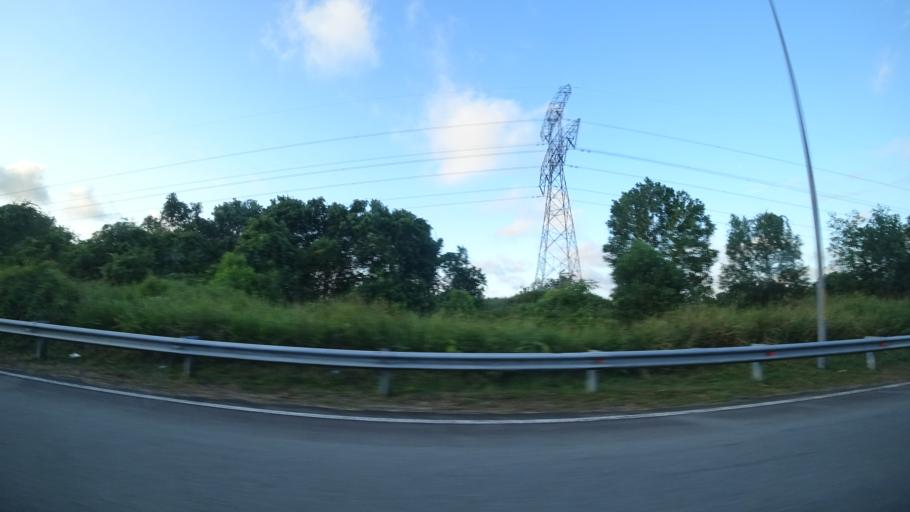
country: BN
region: Tutong
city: Tutong
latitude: 4.8306
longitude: 114.7180
